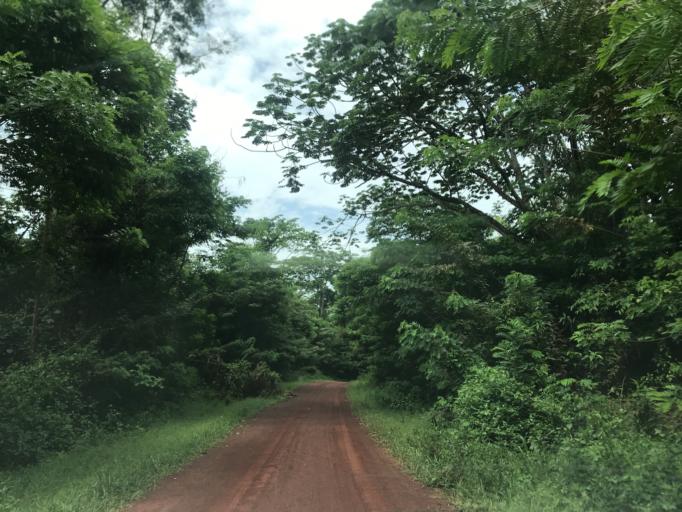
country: CD
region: Eastern Province
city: Buta
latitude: 2.4625
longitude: 24.8729
